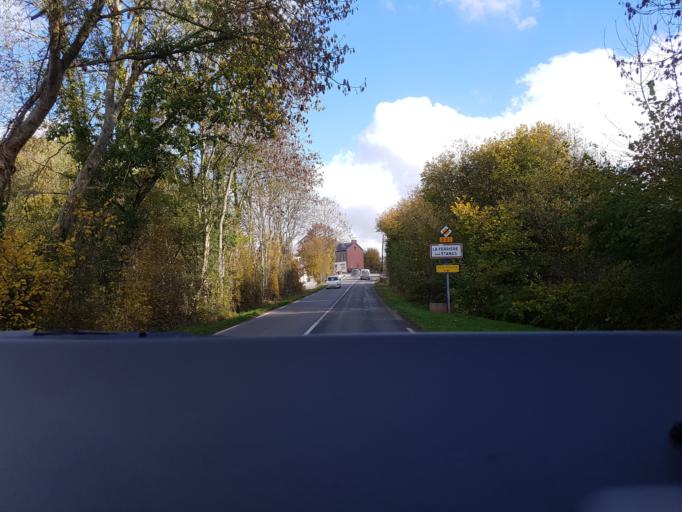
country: FR
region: Lower Normandy
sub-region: Departement de l'Orne
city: La Ferriere-aux-Etangs
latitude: 48.6602
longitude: -0.5215
